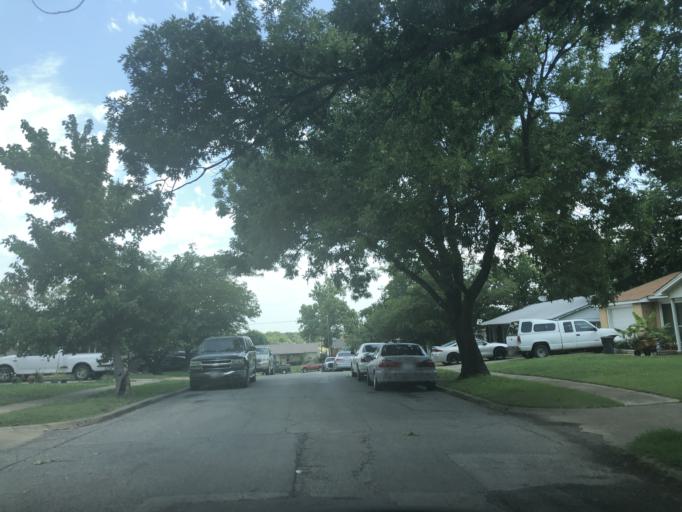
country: US
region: Texas
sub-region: Dallas County
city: Grand Prairie
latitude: 32.7232
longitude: -97.0101
